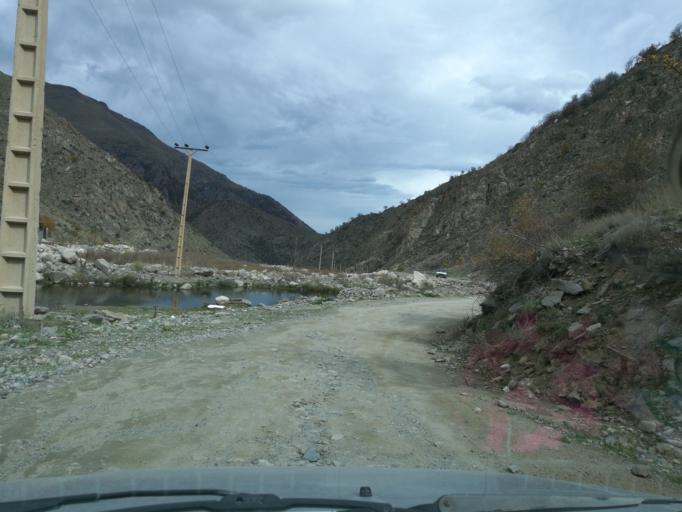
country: IR
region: Mazandaran
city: `Abbasabad
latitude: 36.4281
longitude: 51.0389
